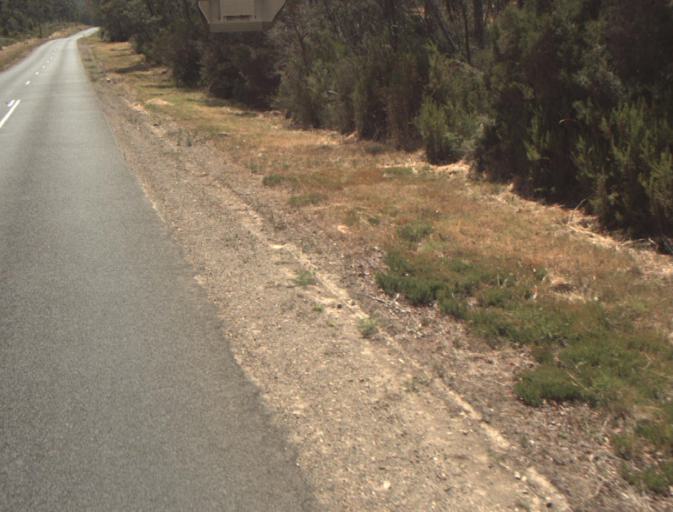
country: AU
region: Tasmania
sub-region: Launceston
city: Mayfield
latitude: -41.2919
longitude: 147.1302
